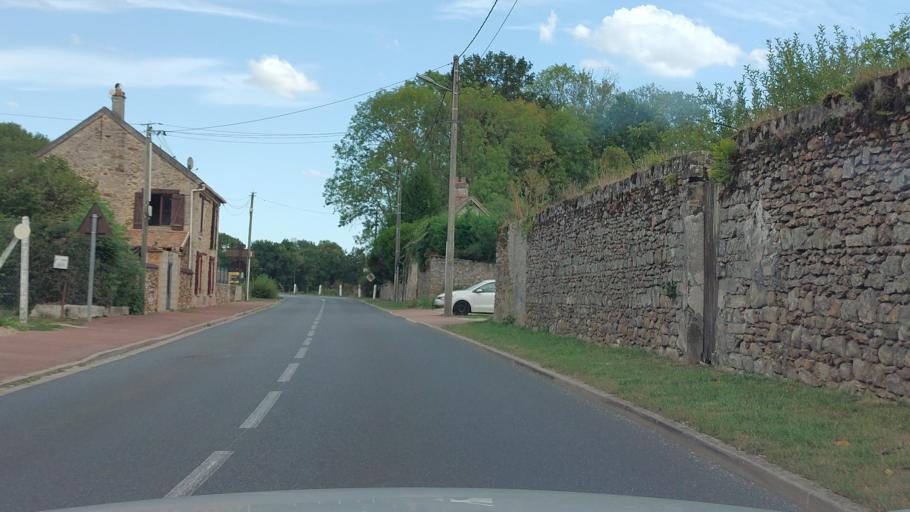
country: FR
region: Ile-de-France
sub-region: Departement de Seine-et-Marne
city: Le Chatelet-en-Brie
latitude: 48.5427
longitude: 2.8102
